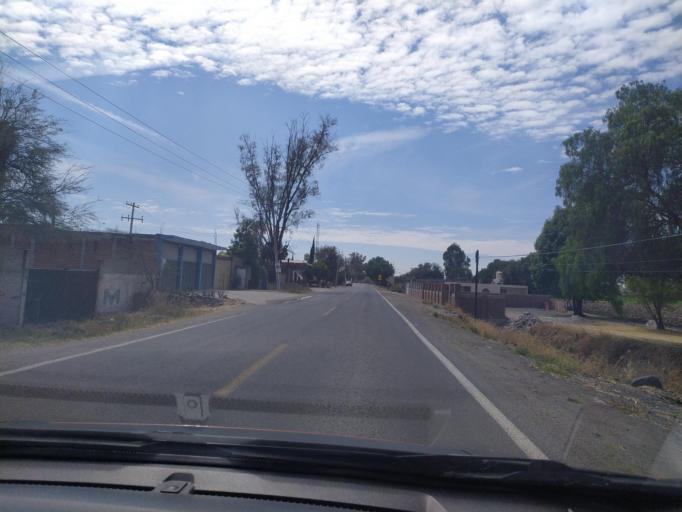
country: MX
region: Guanajuato
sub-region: San Francisco del Rincon
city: San Ignacio de Hidalgo
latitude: 20.8607
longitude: -101.8607
